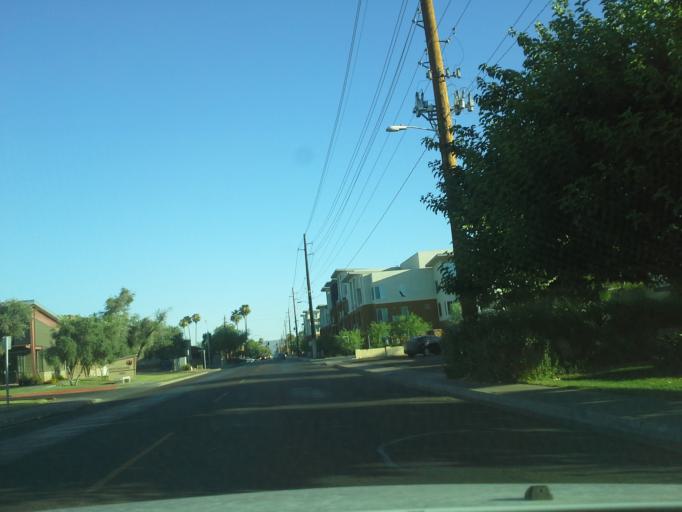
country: US
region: Arizona
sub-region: Maricopa County
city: Phoenix
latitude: 33.4978
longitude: -112.0216
